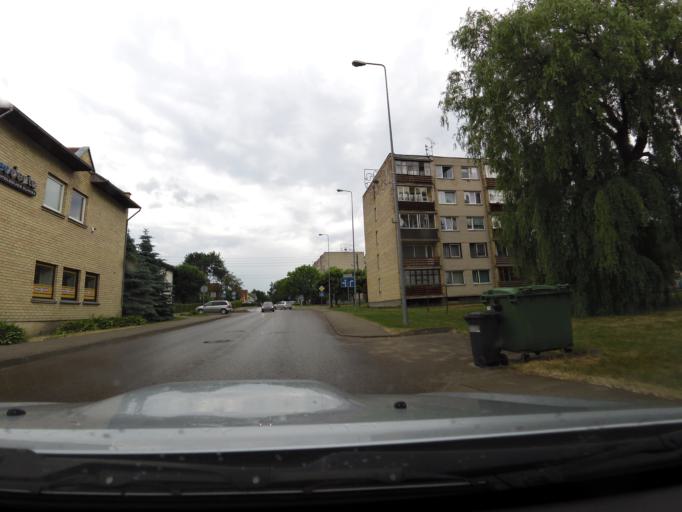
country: LT
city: Vilkaviskis
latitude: 54.6506
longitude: 23.0328
